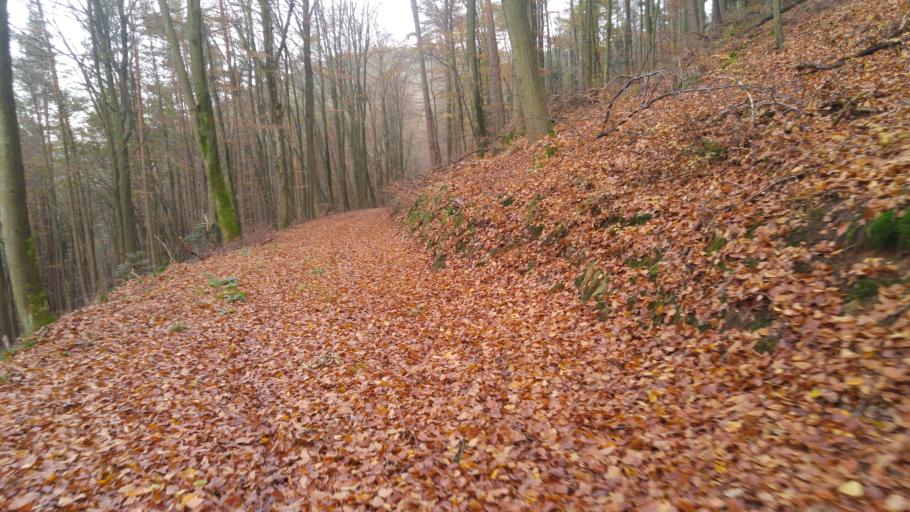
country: DE
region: Rheinland-Pfalz
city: Vorderweidenthal
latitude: 49.1049
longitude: 7.8979
